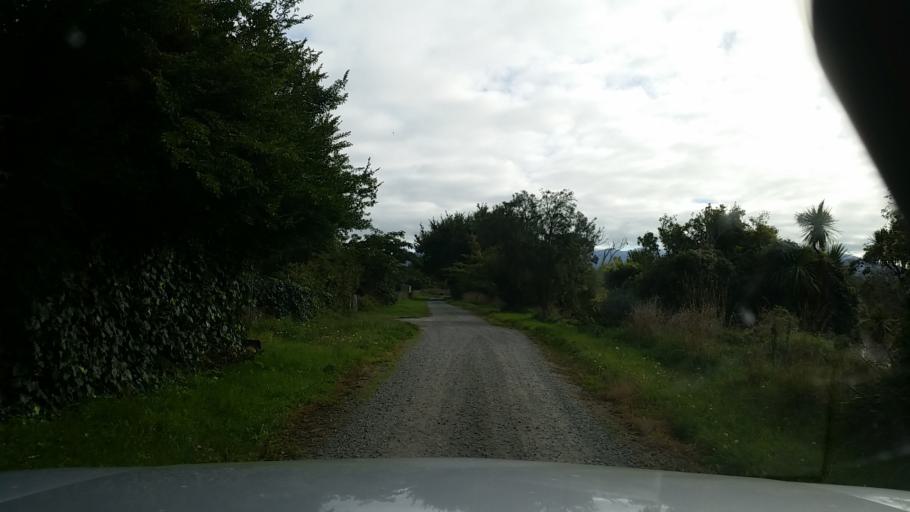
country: NZ
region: Marlborough
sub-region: Marlborough District
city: Blenheim
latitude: -41.4741
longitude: 173.9805
